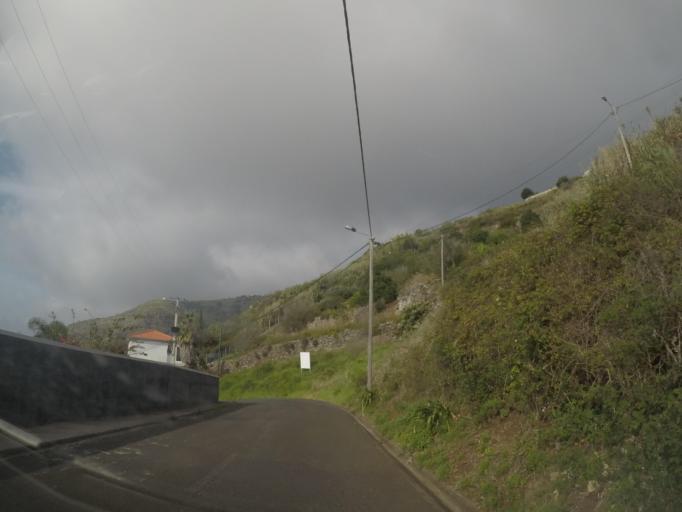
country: PT
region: Madeira
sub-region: Calheta
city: Faja da Ovelha
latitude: 32.7778
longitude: -17.2377
